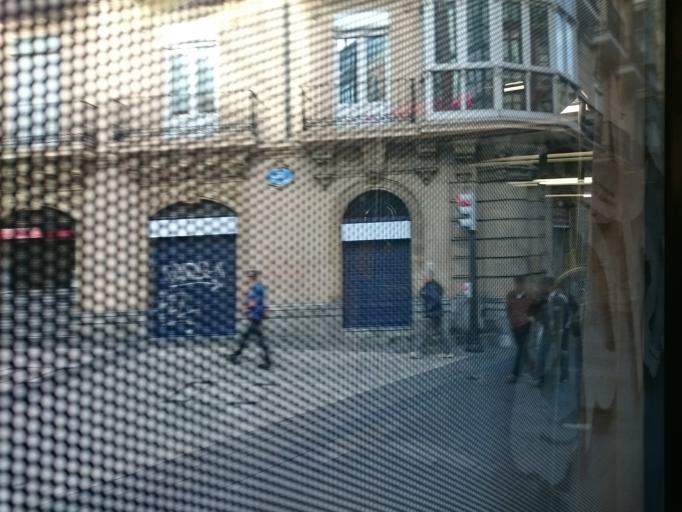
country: ES
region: Basque Country
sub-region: Bizkaia
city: Bilbao
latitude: 43.2619
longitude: -2.9267
